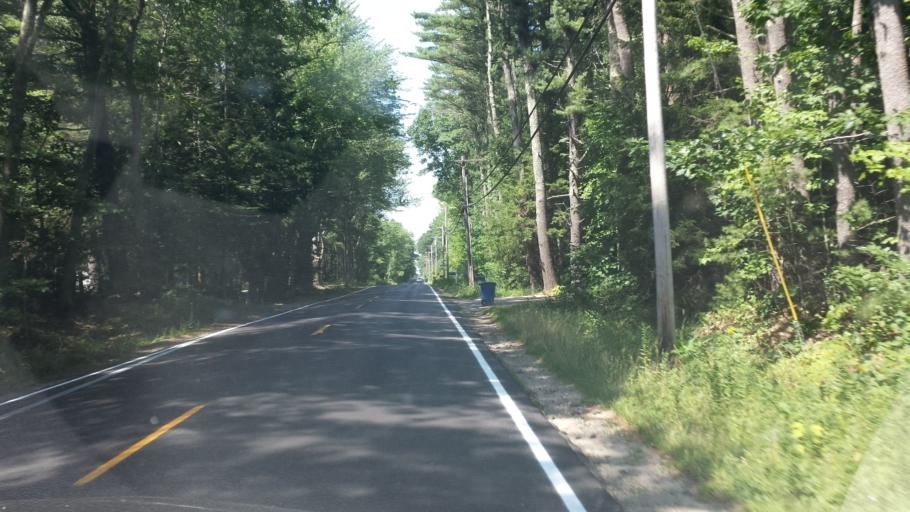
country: US
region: Maine
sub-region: York County
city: Arundel
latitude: 43.3941
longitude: -70.4834
